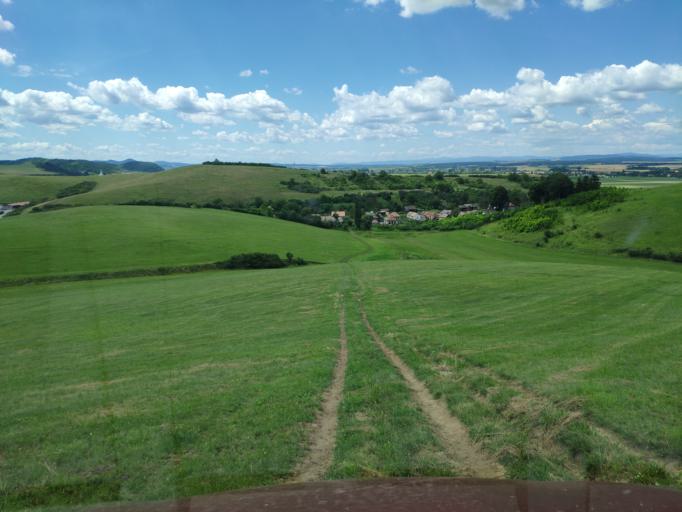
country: HU
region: Borsod-Abauj-Zemplen
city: Ozd
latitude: 48.2768
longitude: 20.2199
